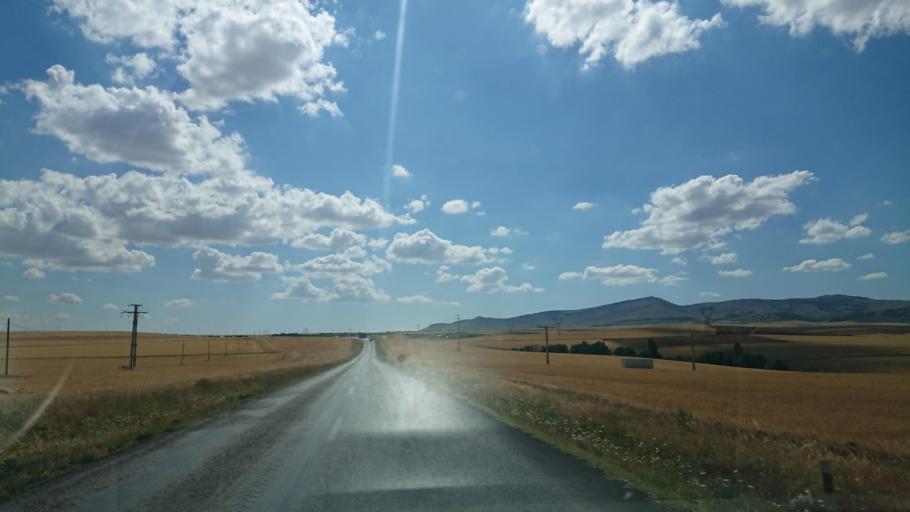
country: TR
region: Kirsehir
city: Kirsehir
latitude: 39.1512
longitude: 34.1034
